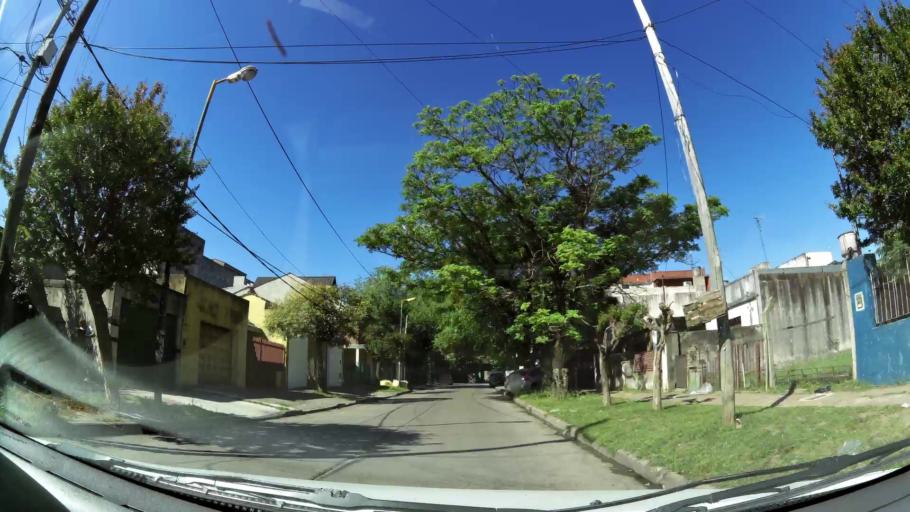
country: AR
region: Buenos Aires
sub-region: Partido de San Isidro
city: San Isidro
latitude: -34.5095
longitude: -58.5790
